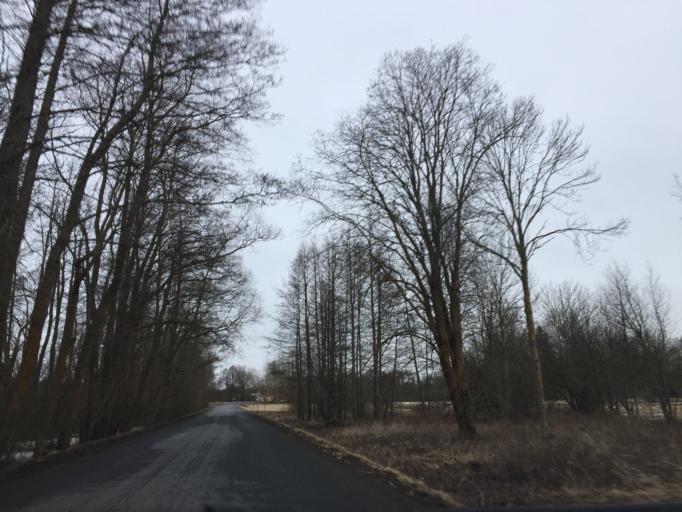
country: EE
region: Laeaene
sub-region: Haapsalu linn
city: Haapsalu
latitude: 58.7852
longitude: 23.4772
